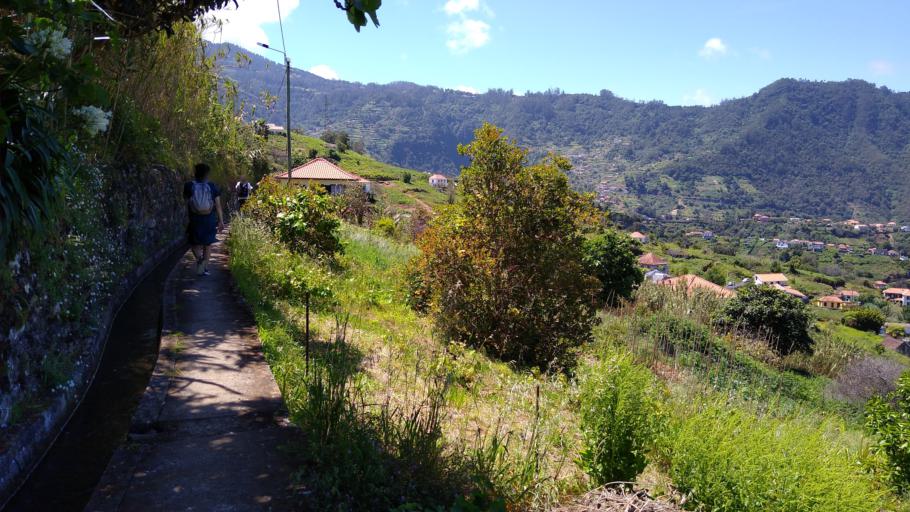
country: PT
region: Madeira
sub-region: Santana
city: Santana
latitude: 32.7673
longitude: -16.8475
